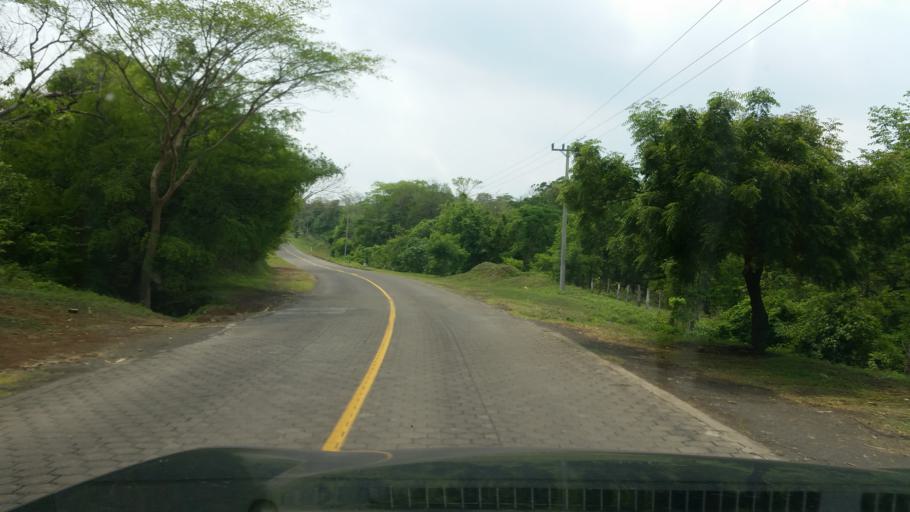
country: NI
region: Managua
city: San Rafael del Sur
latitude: 11.8704
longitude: -86.5147
